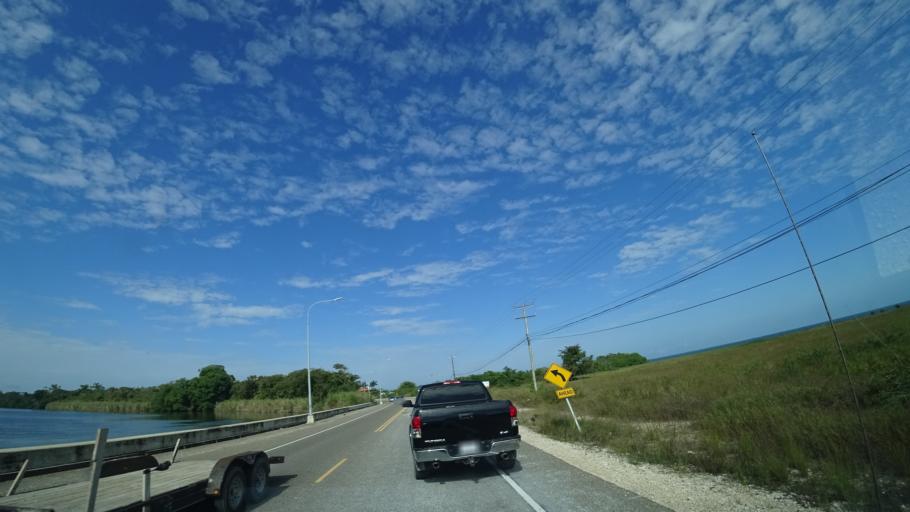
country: BZ
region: Belize
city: Belize City
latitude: 17.5439
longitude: -88.2562
